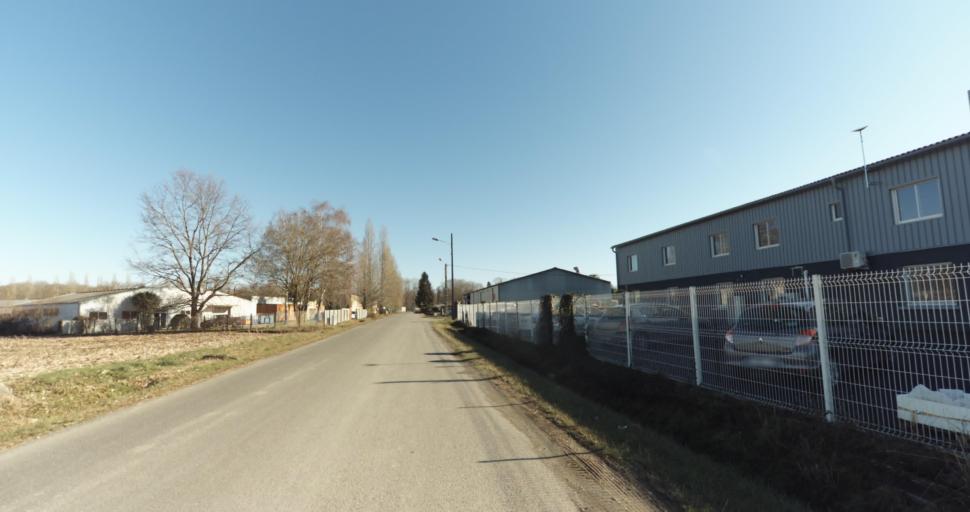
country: FR
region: Aquitaine
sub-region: Departement des Pyrenees-Atlantiques
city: Buros
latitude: 43.3294
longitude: -0.3037
